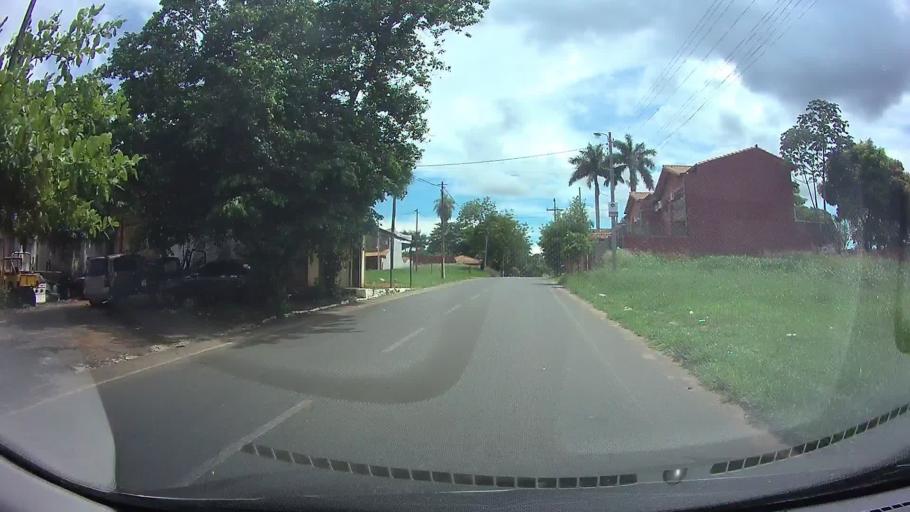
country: PY
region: Central
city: Fernando de la Mora
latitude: -25.3189
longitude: -57.5289
